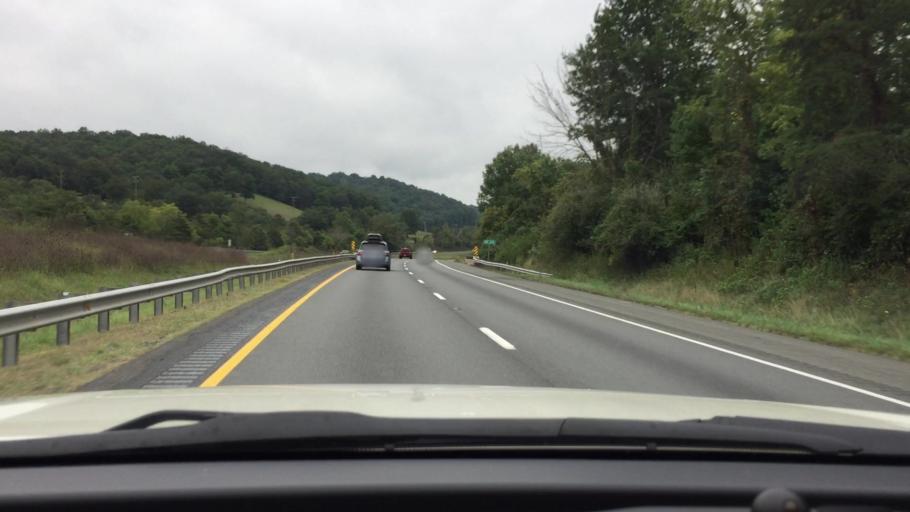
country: US
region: Maryland
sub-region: Washington County
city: Hancock
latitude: 39.6853
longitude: -78.1039
